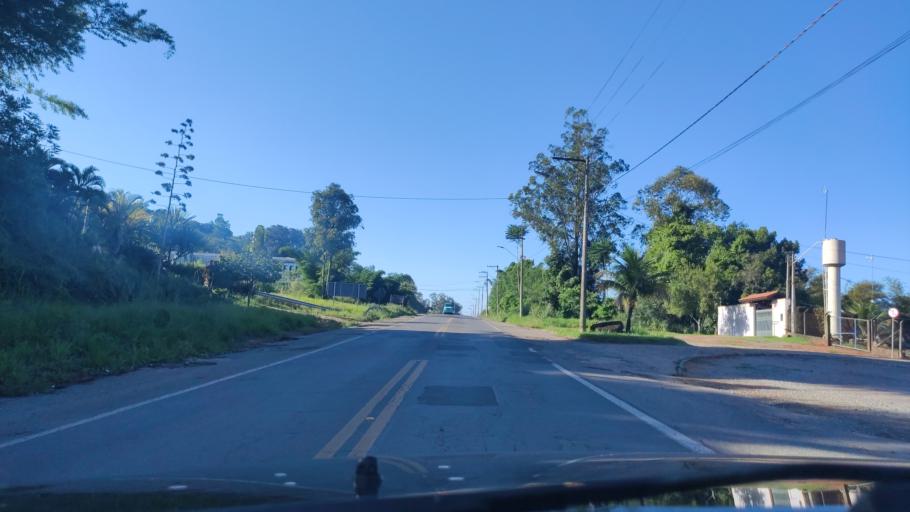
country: BR
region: Sao Paulo
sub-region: Socorro
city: Socorro
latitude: -22.6046
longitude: -46.5256
